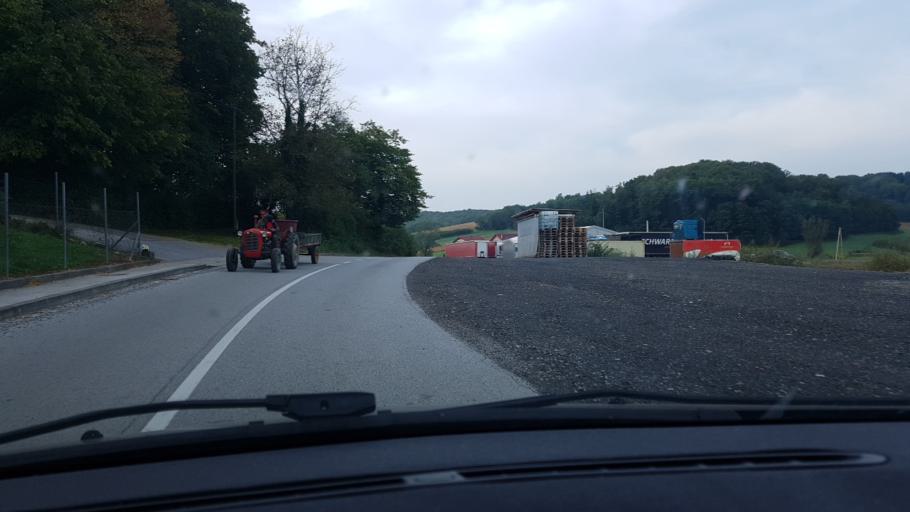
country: HR
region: Krapinsko-Zagorska
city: Mihovljan
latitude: 46.1419
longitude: 15.9640
